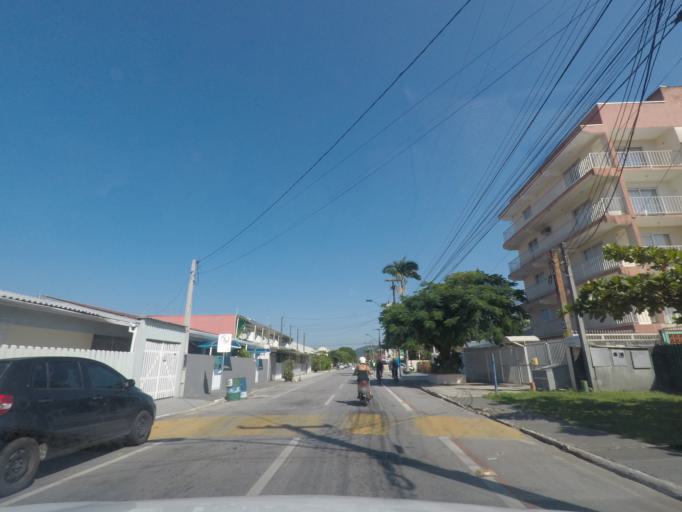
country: BR
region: Parana
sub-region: Guaratuba
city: Guaratuba
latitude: -25.8206
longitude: -48.5345
